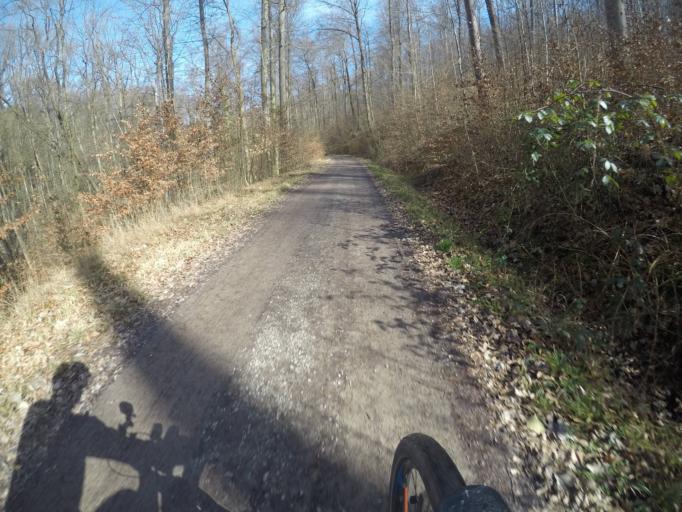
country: DE
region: Baden-Wuerttemberg
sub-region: Regierungsbezirk Stuttgart
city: Korntal
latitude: 48.7934
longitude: 9.1110
